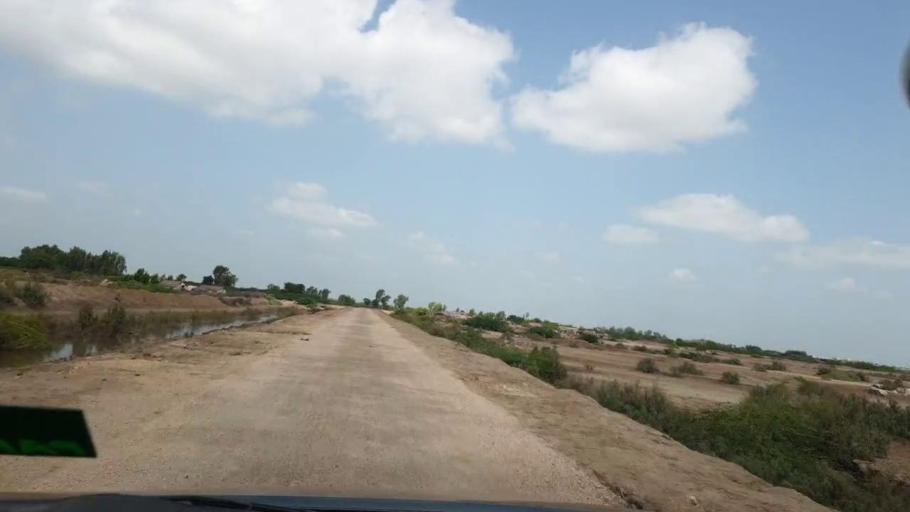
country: PK
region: Sindh
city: Kadhan
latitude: 24.6030
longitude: 69.1209
